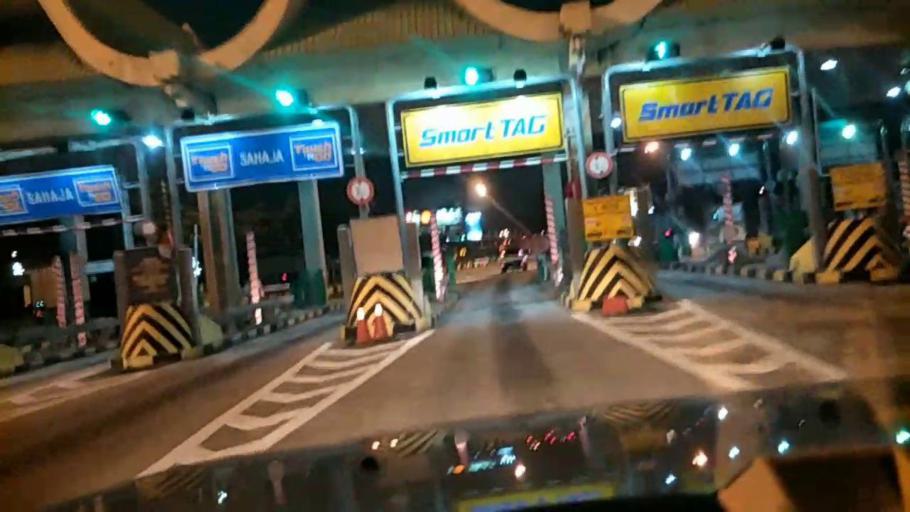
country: MY
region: Penang
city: Juru
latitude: 5.3235
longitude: 100.4365
